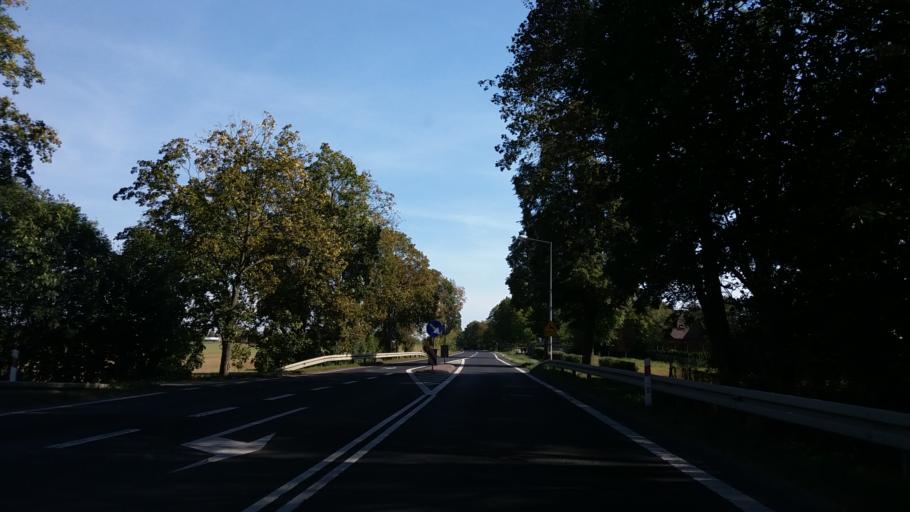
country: PL
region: Greater Poland Voivodeship
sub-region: Powiat miedzychodzki
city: Kwilcz
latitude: 52.5576
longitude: 16.0681
